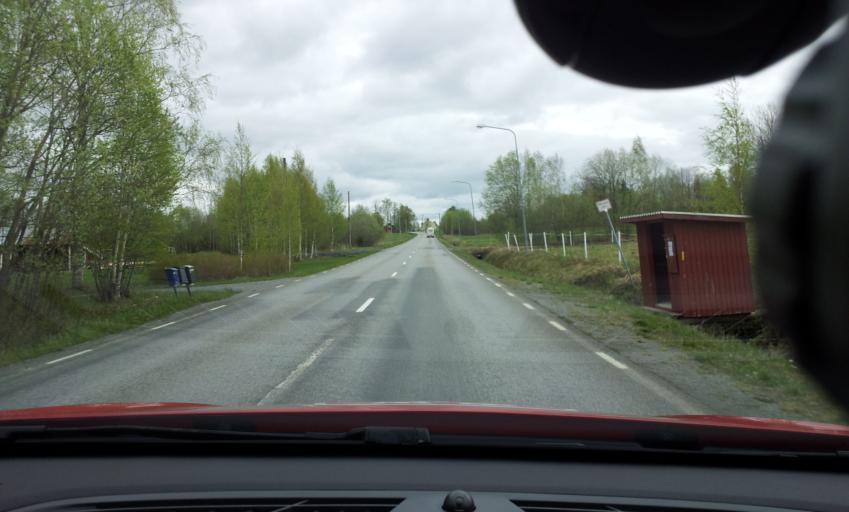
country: SE
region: Jaemtland
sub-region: OEstersunds Kommun
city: Brunflo
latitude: 63.0837
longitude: 14.7557
